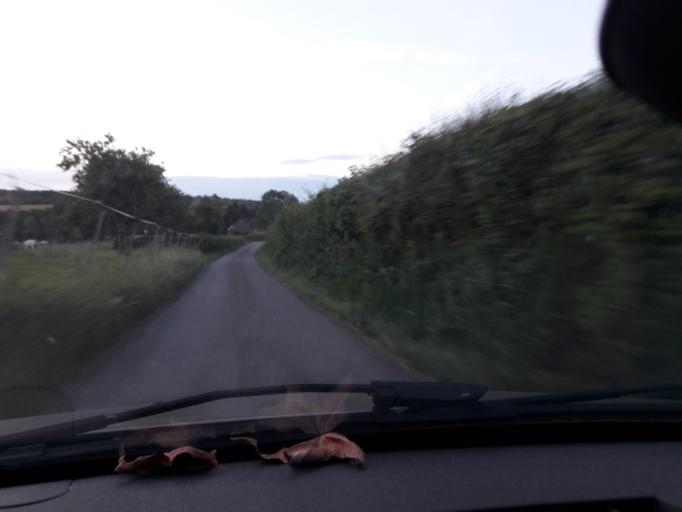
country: BE
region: Wallonia
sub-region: Province du Hainaut
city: Beaumont
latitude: 50.2646
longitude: 4.1871
